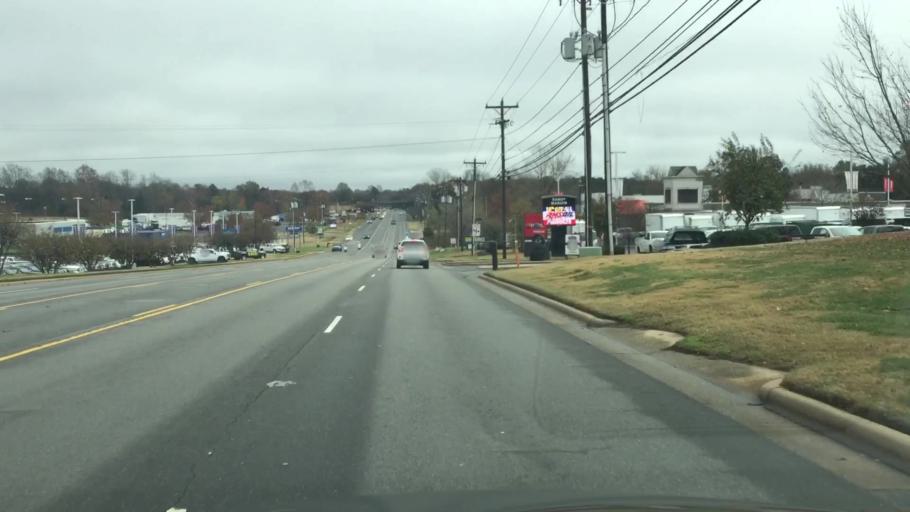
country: US
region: North Carolina
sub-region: Iredell County
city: Mooresville
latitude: 35.5908
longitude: -80.8459
